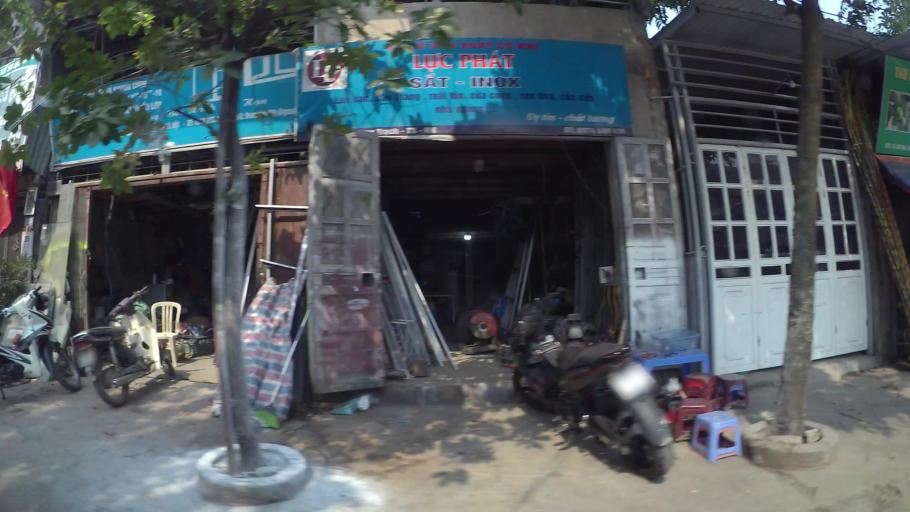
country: VN
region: Ha Noi
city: Thanh Xuan
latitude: 20.9857
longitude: 105.8192
